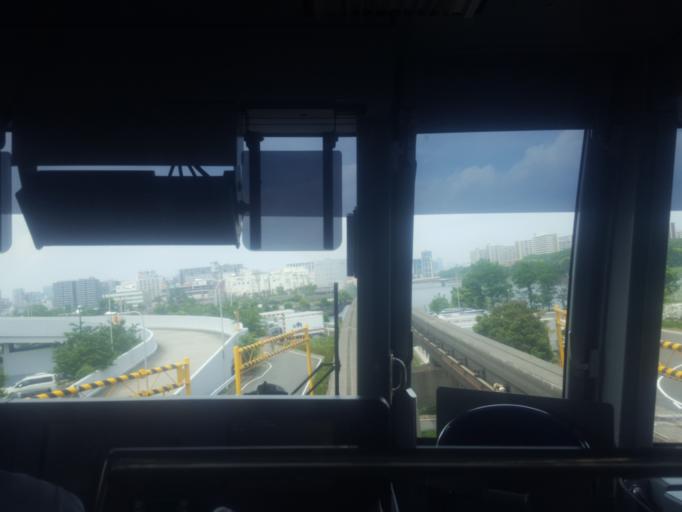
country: JP
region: Kanagawa
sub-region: Kawasaki-shi
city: Kawasaki
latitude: 35.5884
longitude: 139.7466
